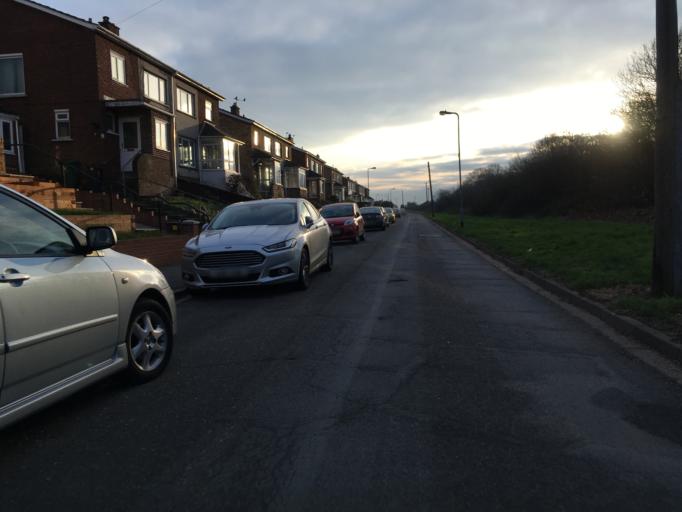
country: GB
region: Wales
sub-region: Cardiff
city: Cardiff
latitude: 51.5160
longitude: -3.1327
